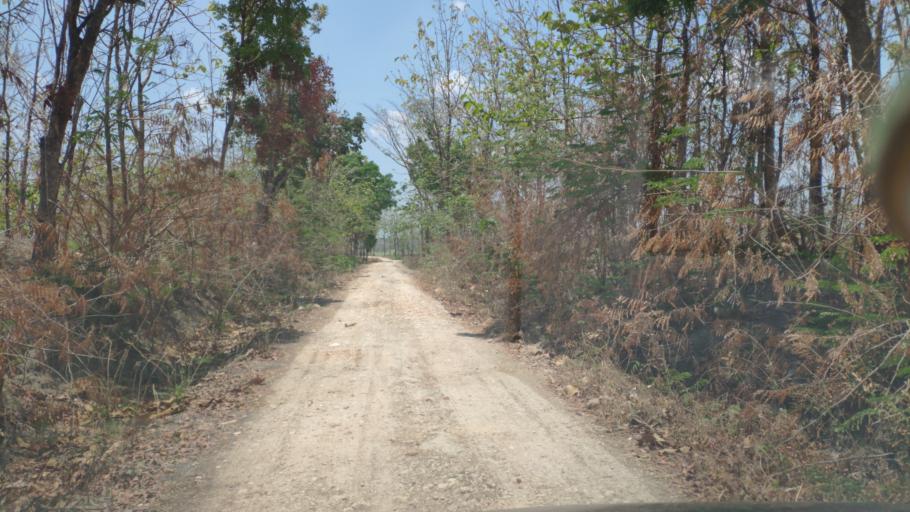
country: ID
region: West Java
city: Ngawi
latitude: -7.3267
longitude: 111.3600
